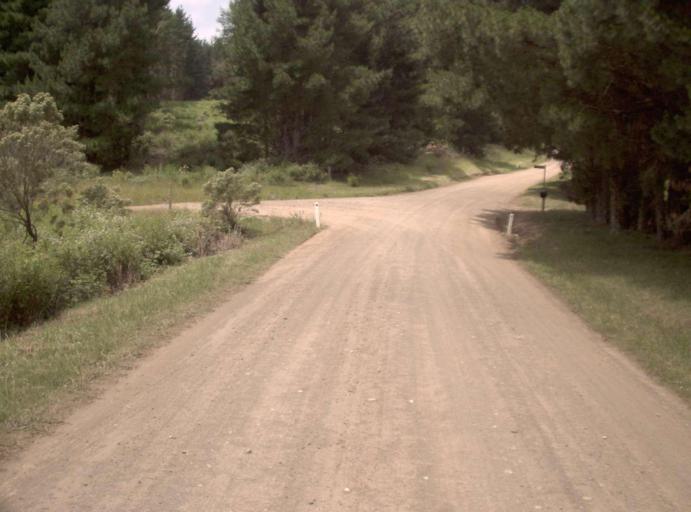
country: AU
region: Victoria
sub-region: Latrobe
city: Traralgon
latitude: -38.4098
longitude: 146.6314
